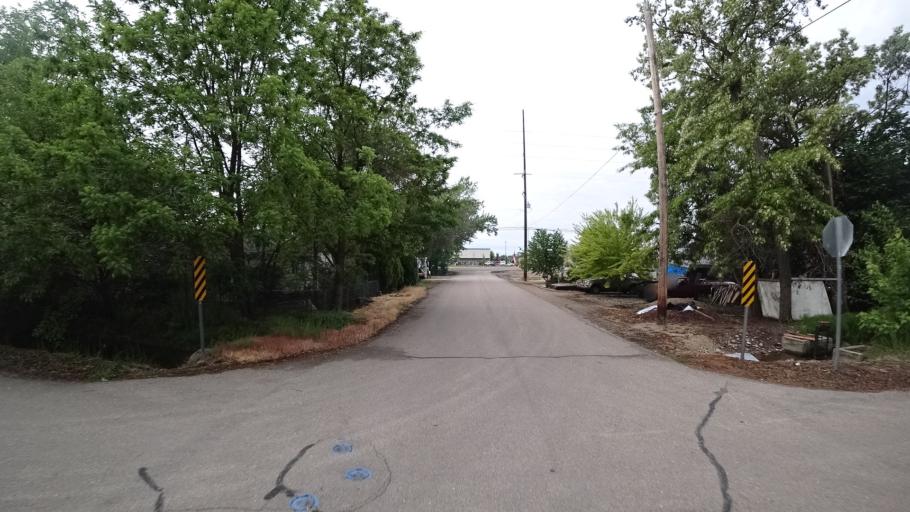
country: US
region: Idaho
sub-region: Ada County
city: Star
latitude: 43.6929
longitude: -116.4956
